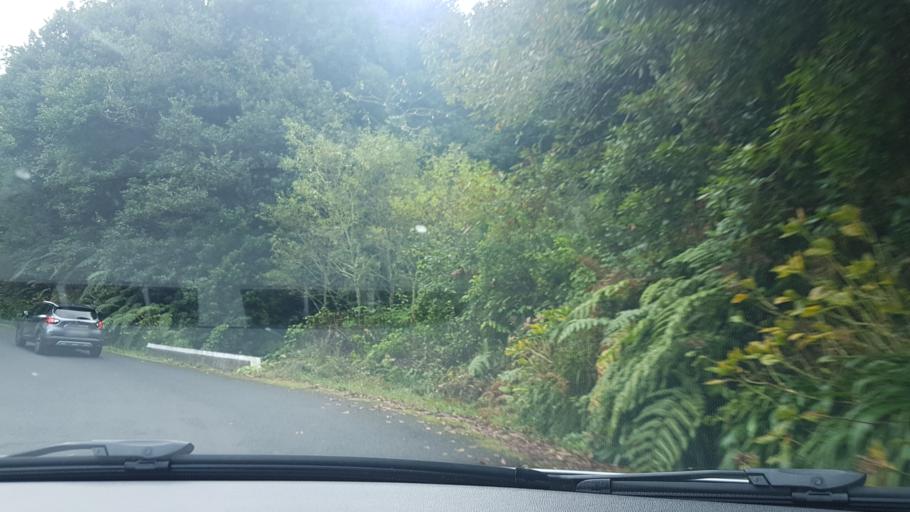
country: PT
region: Madeira
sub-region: Sao Vicente
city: Sao Vicente
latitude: 32.7631
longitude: -17.0222
